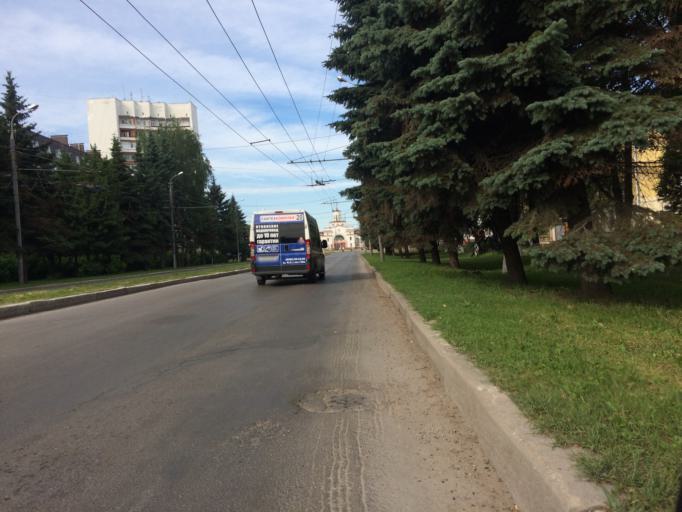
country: RU
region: Mariy-El
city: Yoshkar-Ola
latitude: 56.6234
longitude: 47.8841
